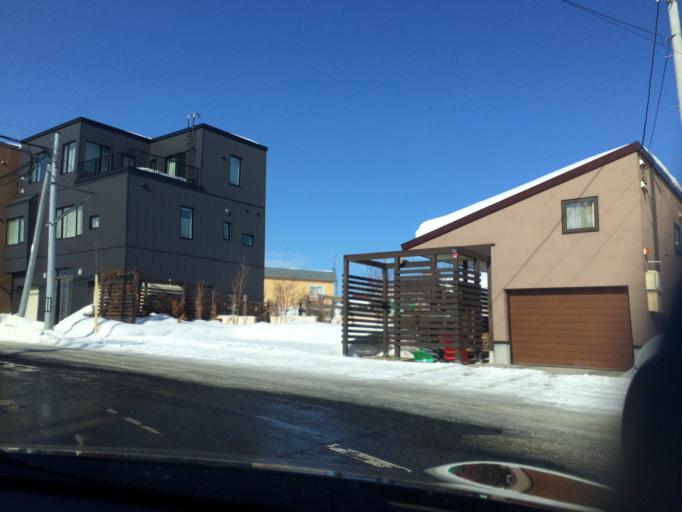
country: JP
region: Hokkaido
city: Ebetsu
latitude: 43.0398
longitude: 141.4880
